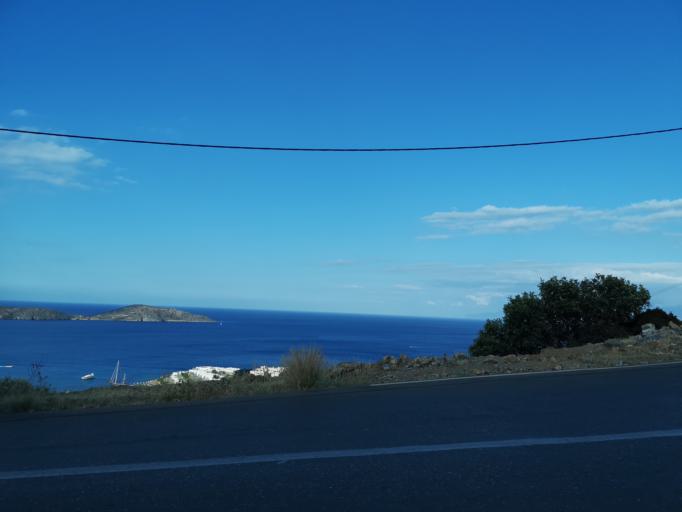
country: GR
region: Crete
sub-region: Nomos Lasithiou
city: Skhisma
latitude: 35.2387
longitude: 25.7269
